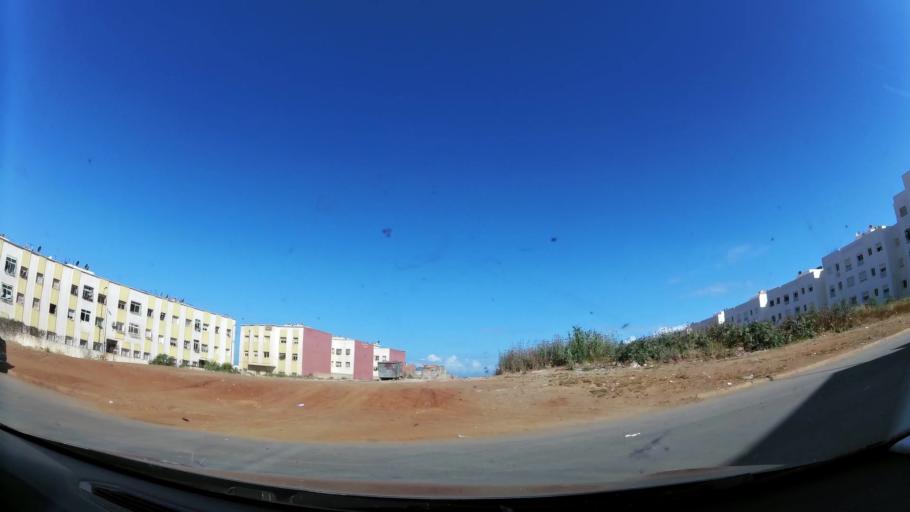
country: MA
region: Rabat-Sale-Zemmour-Zaer
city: Sale
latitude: 34.0585
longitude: -6.8116
